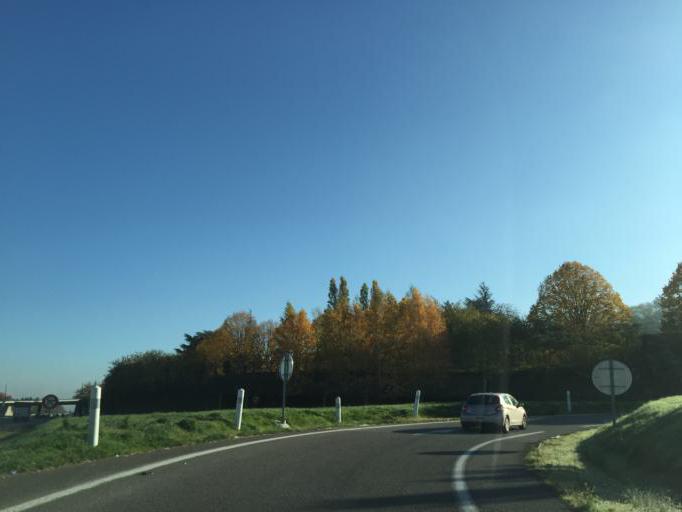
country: FR
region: Rhone-Alpes
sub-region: Departement du Rhone
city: Saint-Genis-Laval
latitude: 45.6779
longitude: 4.7915
